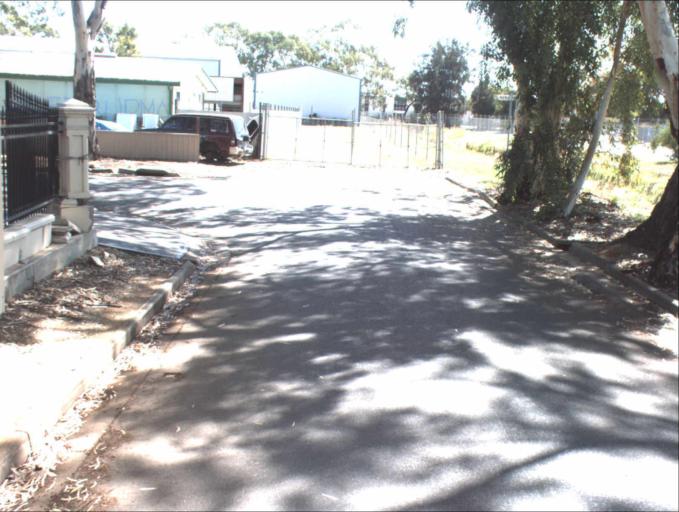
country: AU
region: South Australia
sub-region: Charles Sturt
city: Woodville North
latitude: -34.8478
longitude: 138.5564
